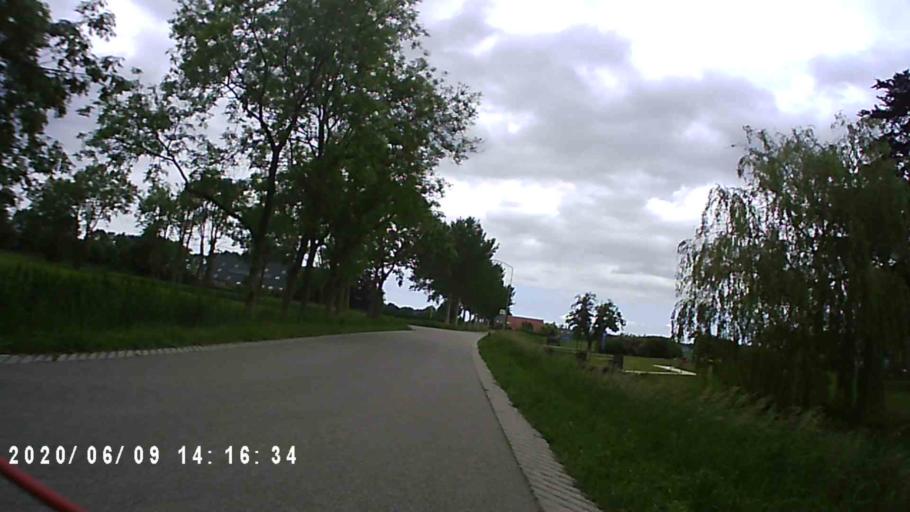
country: NL
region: Groningen
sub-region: Gemeente Bedum
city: Bedum
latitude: 53.2803
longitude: 6.5923
